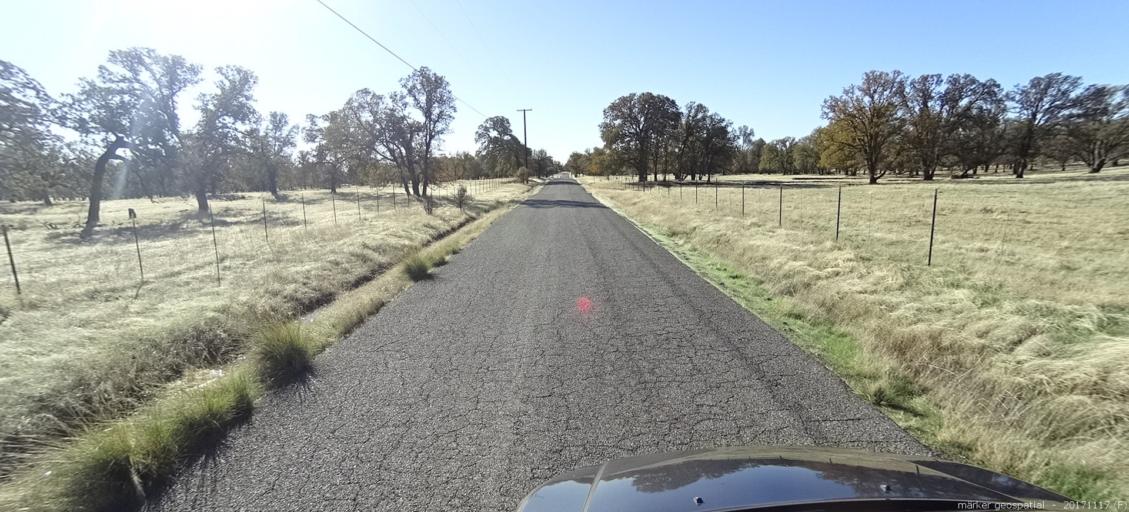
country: US
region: California
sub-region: Shasta County
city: Palo Cedro
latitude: 40.4717
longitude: -122.1909
